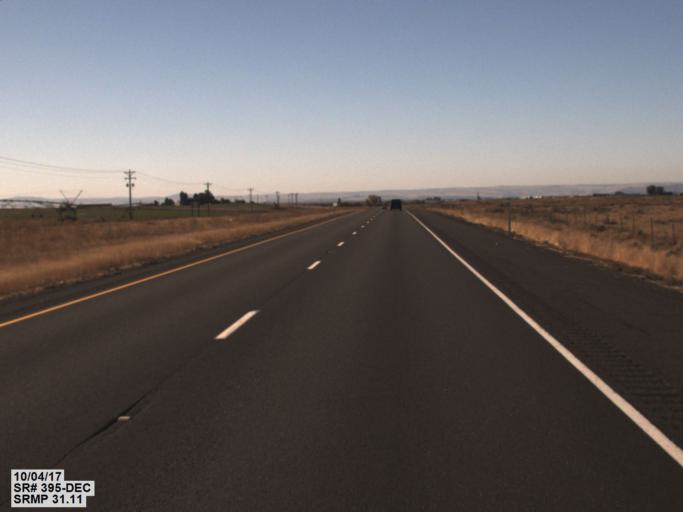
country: US
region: Washington
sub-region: Franklin County
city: Pasco
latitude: 46.3705
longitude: -119.0798
